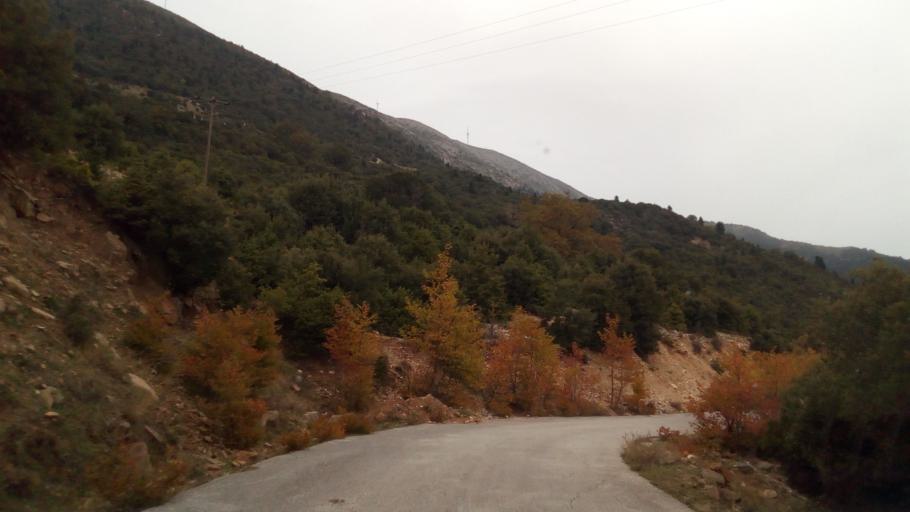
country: GR
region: West Greece
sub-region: Nomos Aitolias kai Akarnanias
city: Thermo
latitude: 38.6035
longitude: 21.8275
